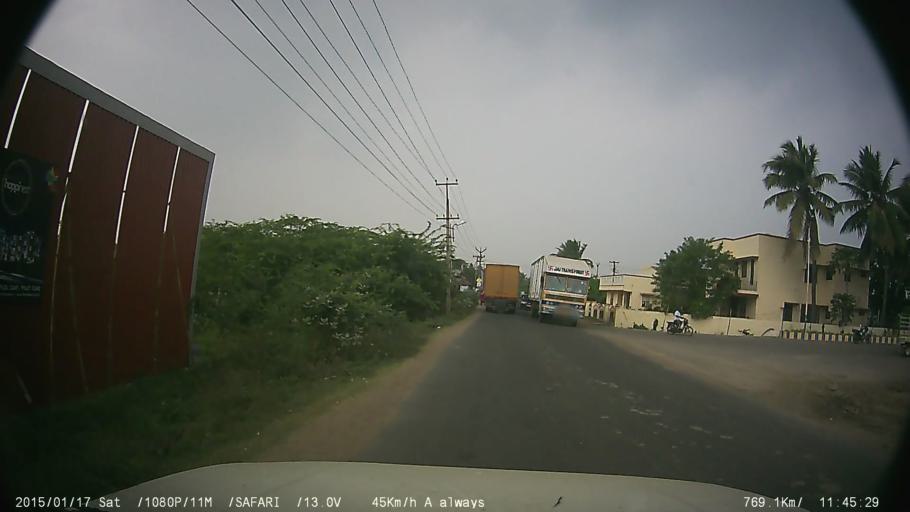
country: IN
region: Tamil Nadu
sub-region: Kancheepuram
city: Singapperumalkovil
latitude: 12.7668
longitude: 79.9971
